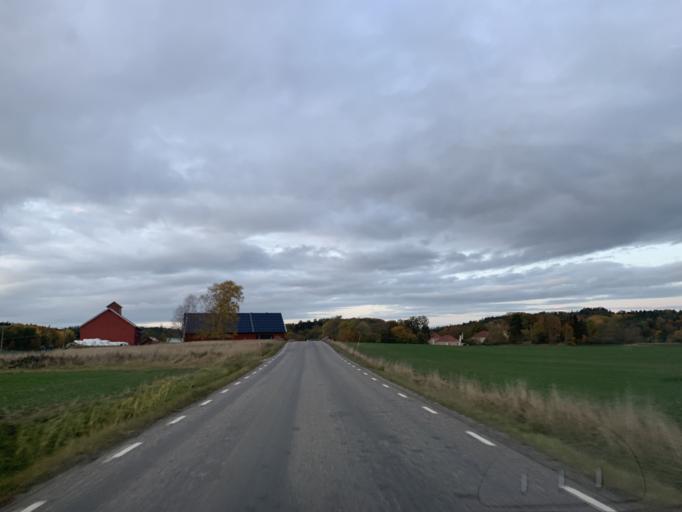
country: SE
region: Stockholm
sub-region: Nynashamns Kommun
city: Osmo
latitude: 58.9547
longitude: 17.7668
